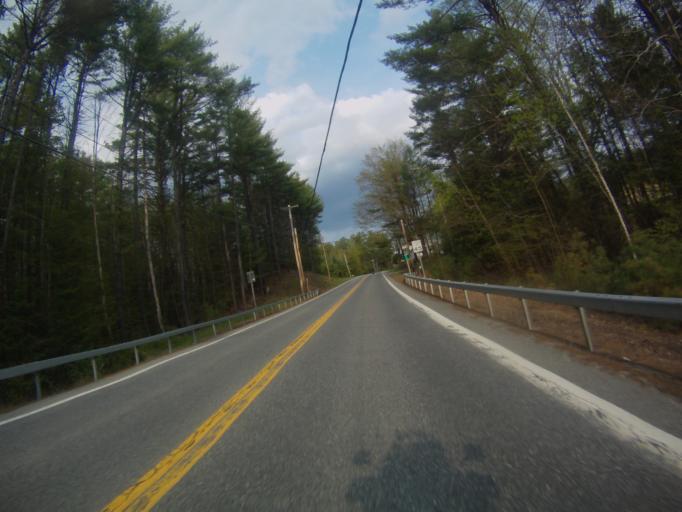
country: US
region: New York
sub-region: Warren County
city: Warrensburg
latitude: 43.6631
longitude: -73.8515
